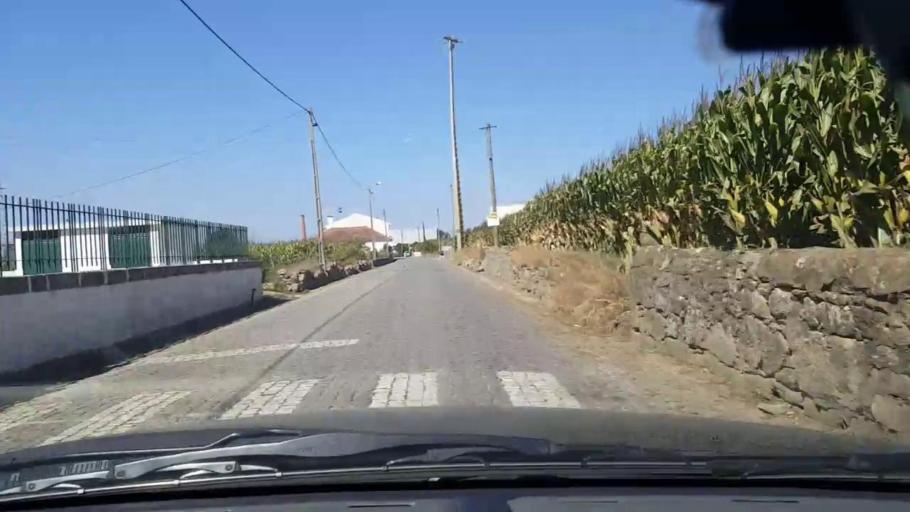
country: PT
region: Porto
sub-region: Matosinhos
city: Lavra
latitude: 41.2783
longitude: -8.7125
